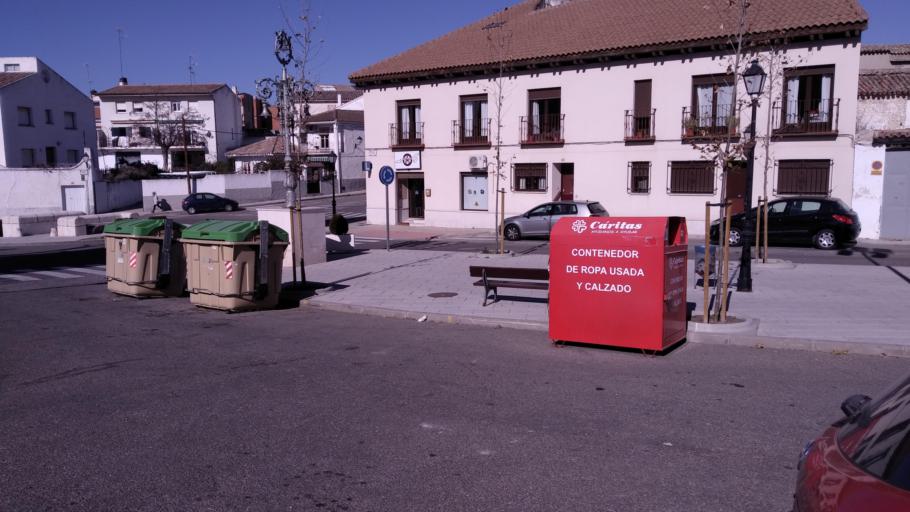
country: ES
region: Castille-La Mancha
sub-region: Province of Toledo
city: Esquivias
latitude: 40.1027
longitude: -3.7673
